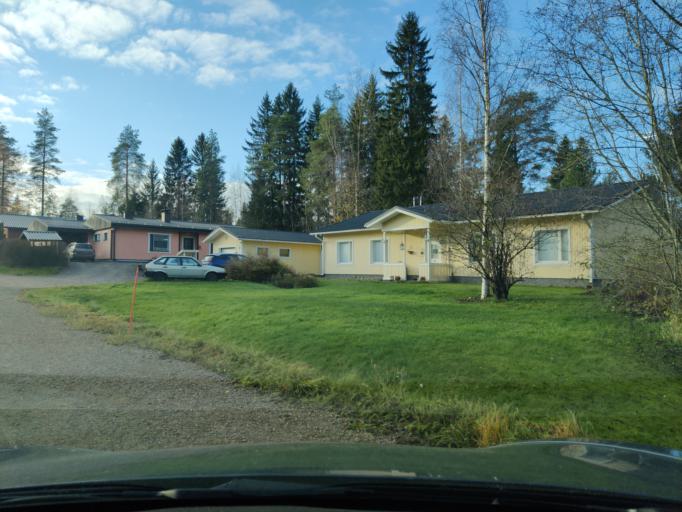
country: FI
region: Northern Savo
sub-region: Ylae-Savo
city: Kiuruvesi
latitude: 63.6450
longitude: 26.6377
